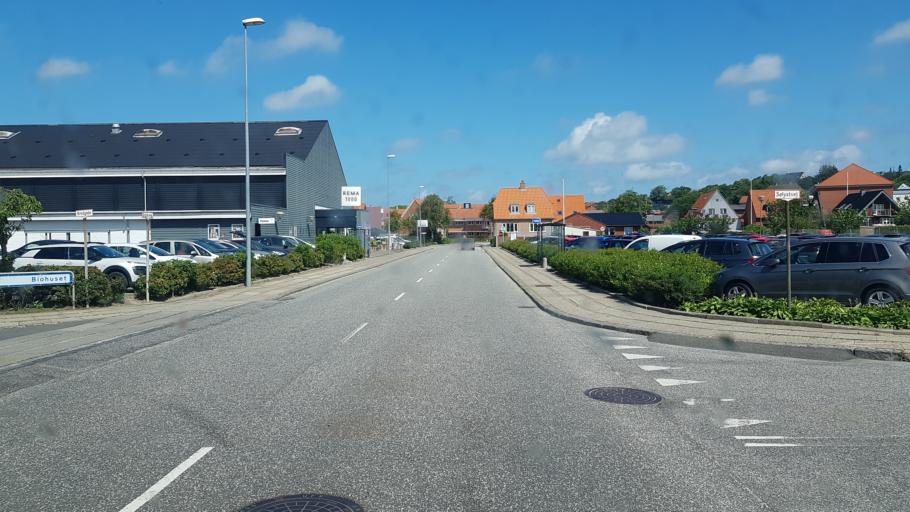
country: DK
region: Central Jutland
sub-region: Lemvig Kommune
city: Lemvig
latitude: 56.5479
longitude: 8.3130
